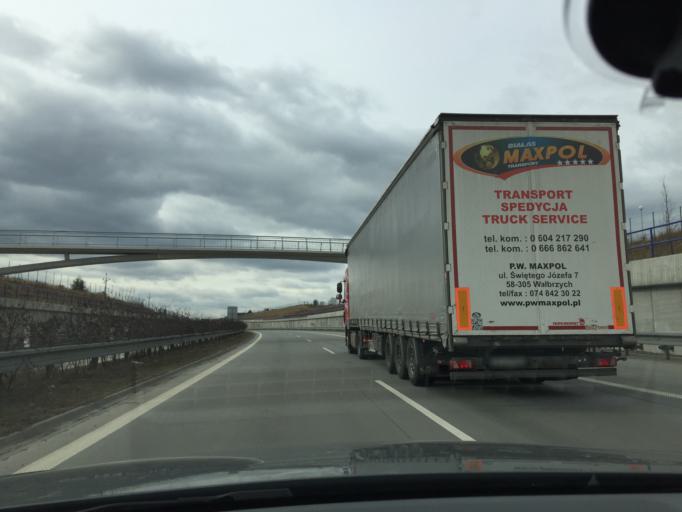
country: CZ
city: Sviadnov
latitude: 49.6682
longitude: 18.3071
